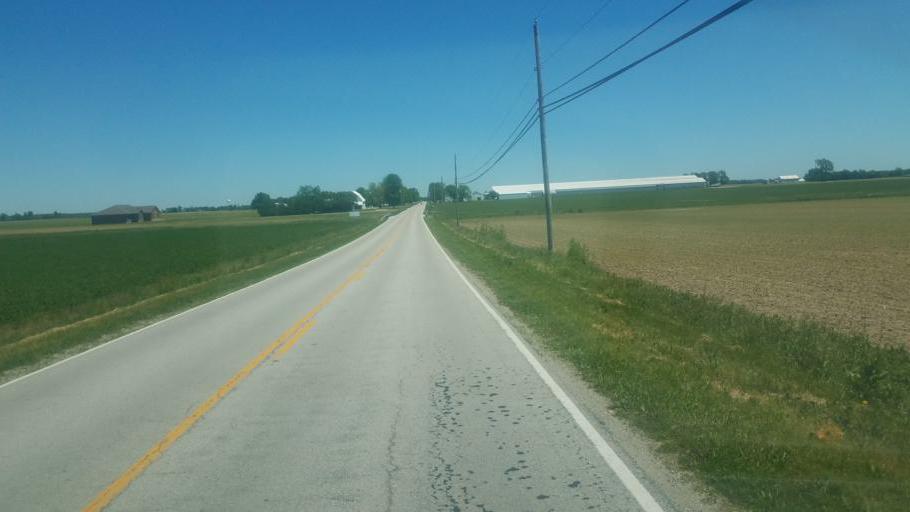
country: US
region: Ohio
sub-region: Darke County
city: Versailles
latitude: 40.2262
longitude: -84.4451
